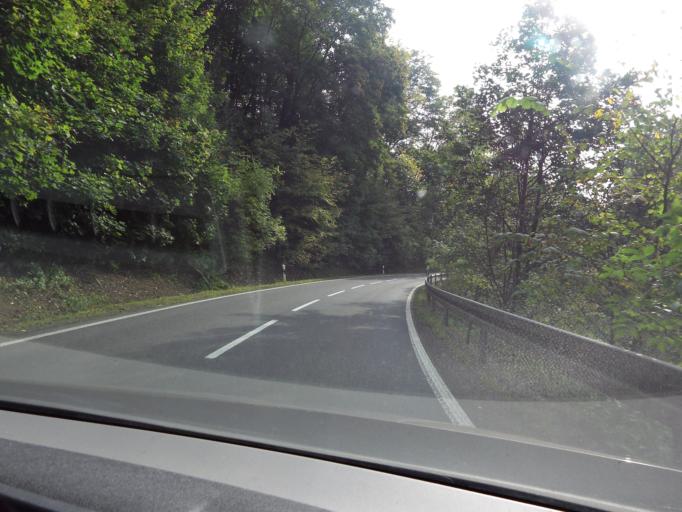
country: DE
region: Thuringia
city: Brotterode
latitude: 50.8034
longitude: 10.4330
